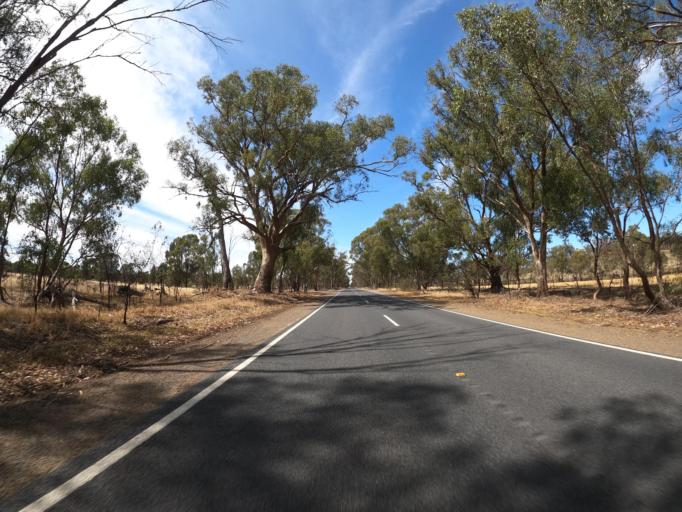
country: AU
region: Victoria
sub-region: Benalla
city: Benalla
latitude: -36.3683
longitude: 145.9712
